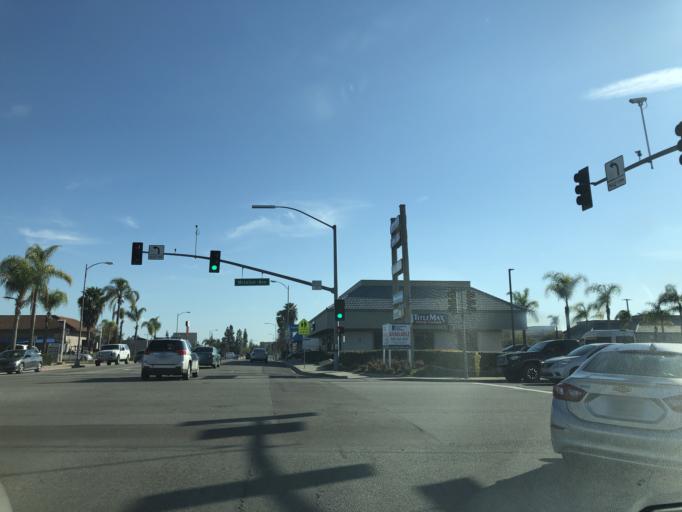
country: US
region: California
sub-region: San Diego County
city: Escondido
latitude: 33.1292
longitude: -117.0896
